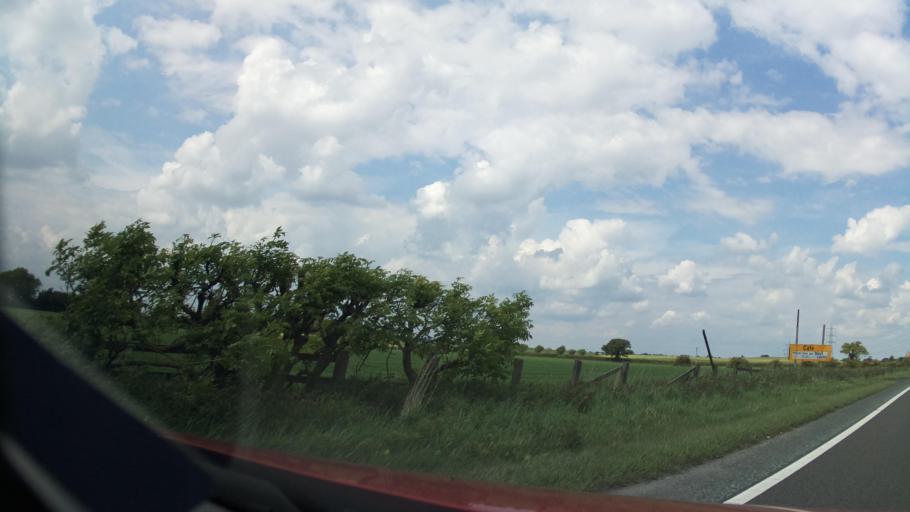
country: GB
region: England
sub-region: North Yorkshire
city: Northallerton
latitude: 54.3434
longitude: -1.3321
